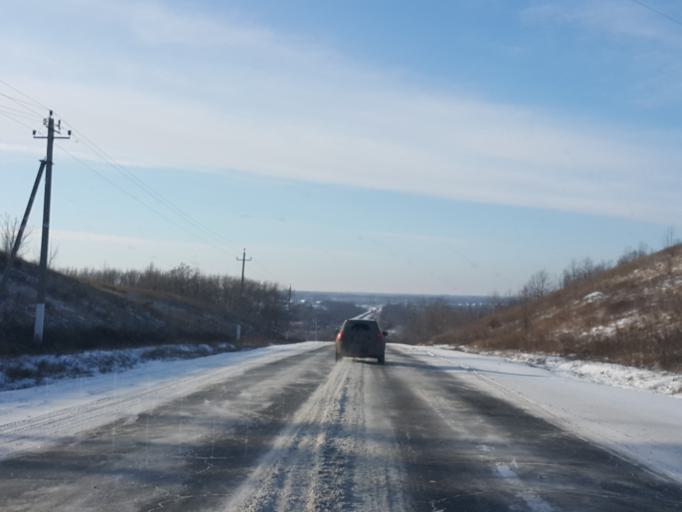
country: RU
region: Tambov
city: Znamenka
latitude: 52.4180
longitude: 41.4893
